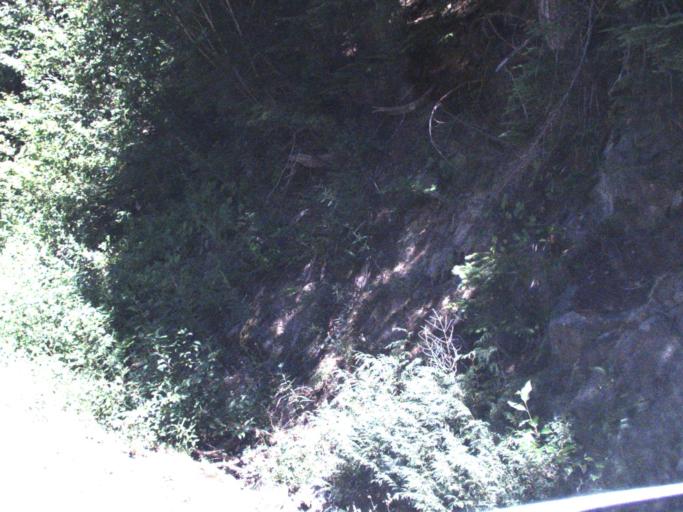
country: US
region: Washington
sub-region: King County
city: Enumclaw
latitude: 46.8398
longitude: -121.5309
